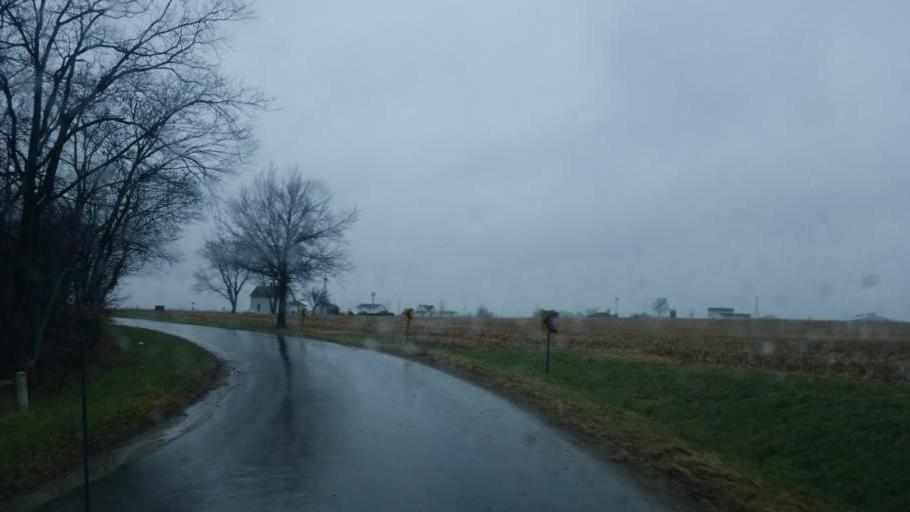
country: US
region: Indiana
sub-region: Adams County
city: Geneva
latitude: 40.6153
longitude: -84.9343
